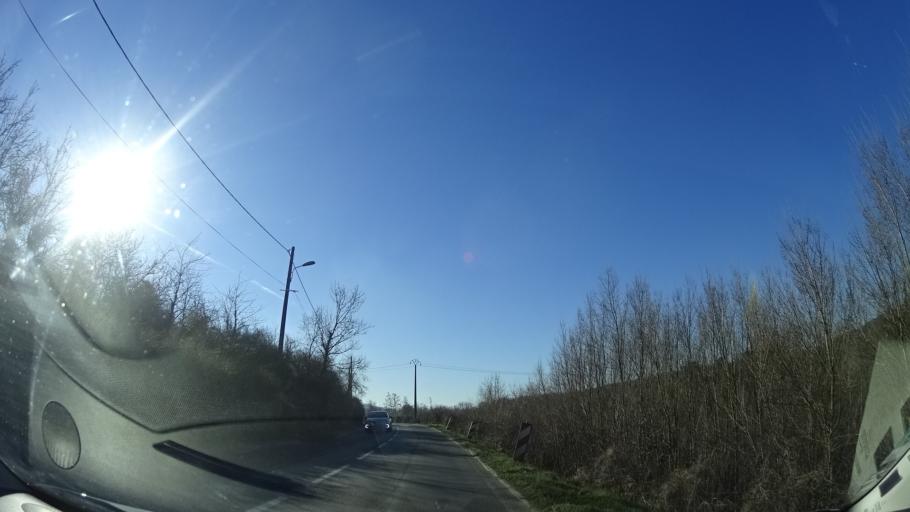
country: FR
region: Poitou-Charentes
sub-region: Departement des Deux-Sevres
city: Airvault
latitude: 46.8213
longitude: -0.1459
